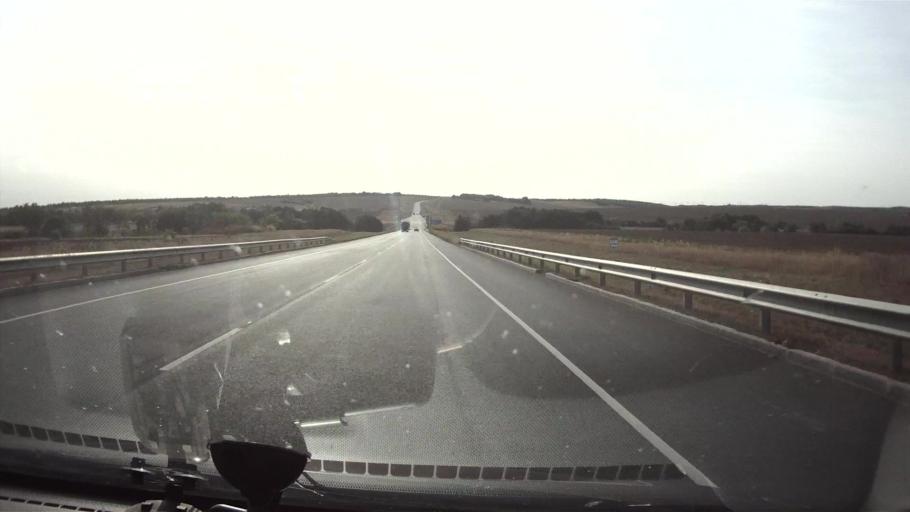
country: RU
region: Saratov
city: Yelshanka
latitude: 51.8276
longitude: 46.3996
